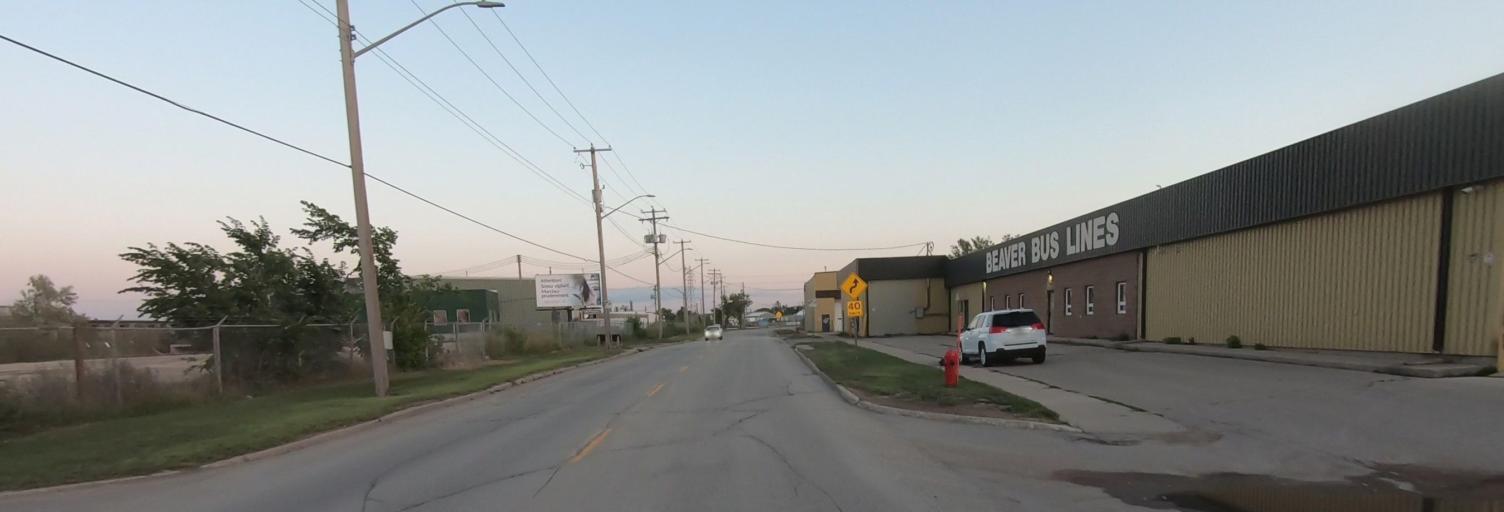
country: CA
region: Manitoba
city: Winnipeg
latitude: 49.8916
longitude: -97.1033
